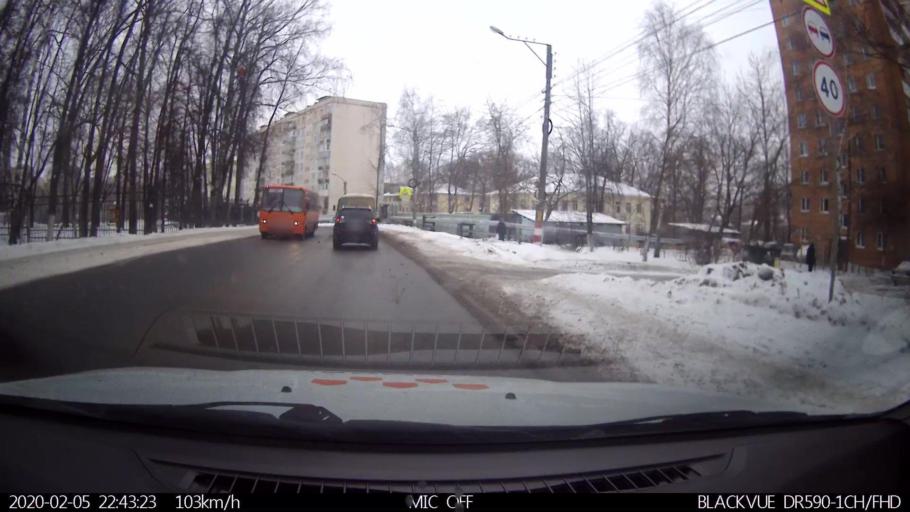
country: RU
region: Nizjnij Novgorod
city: Imeni Stepana Razina
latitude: 54.7129
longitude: 44.3759
